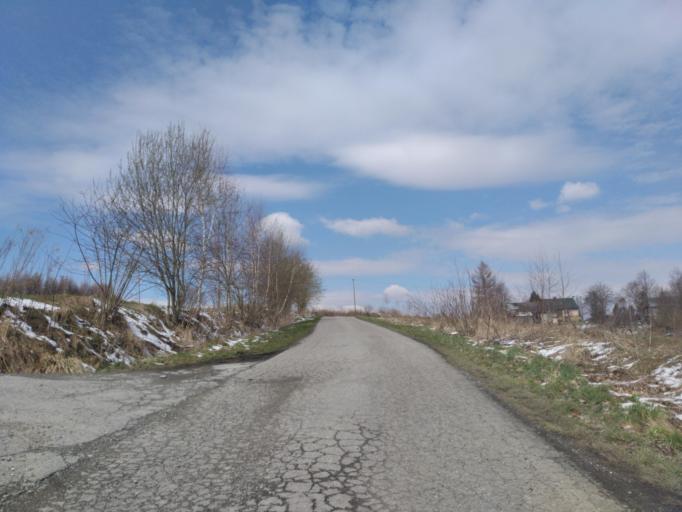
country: PL
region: Subcarpathian Voivodeship
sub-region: Powiat ropczycko-sedziszowski
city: Ropczyce
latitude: 50.0051
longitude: 21.5953
